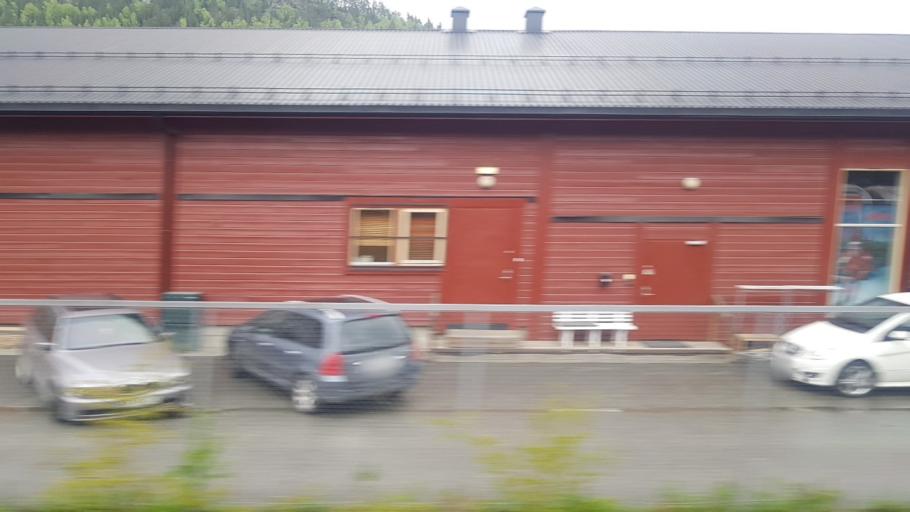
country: NO
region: Oppland
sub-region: Nord-Fron
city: Vinstra
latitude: 61.5808
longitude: 9.7631
